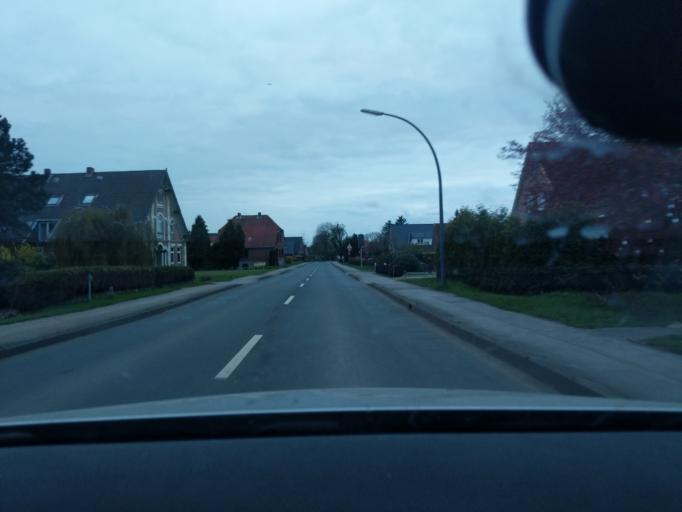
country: DE
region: Lower Saxony
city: Neu Wulmstorf
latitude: 53.5143
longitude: 9.7996
